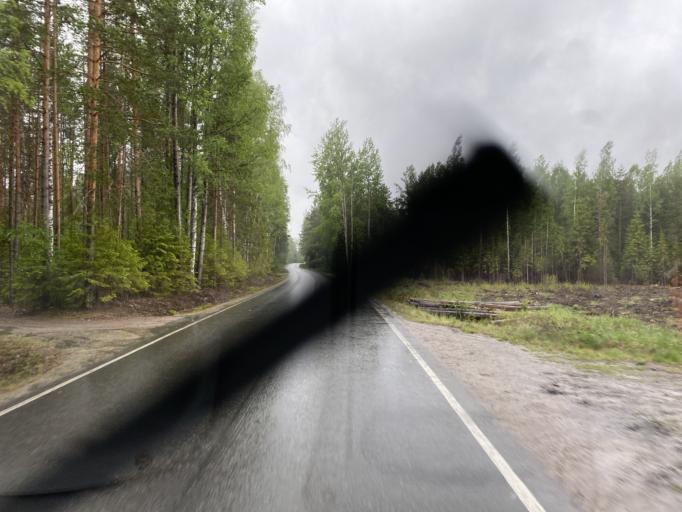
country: FI
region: Haeme
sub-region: Forssa
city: Humppila
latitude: 61.0857
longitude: 23.3097
